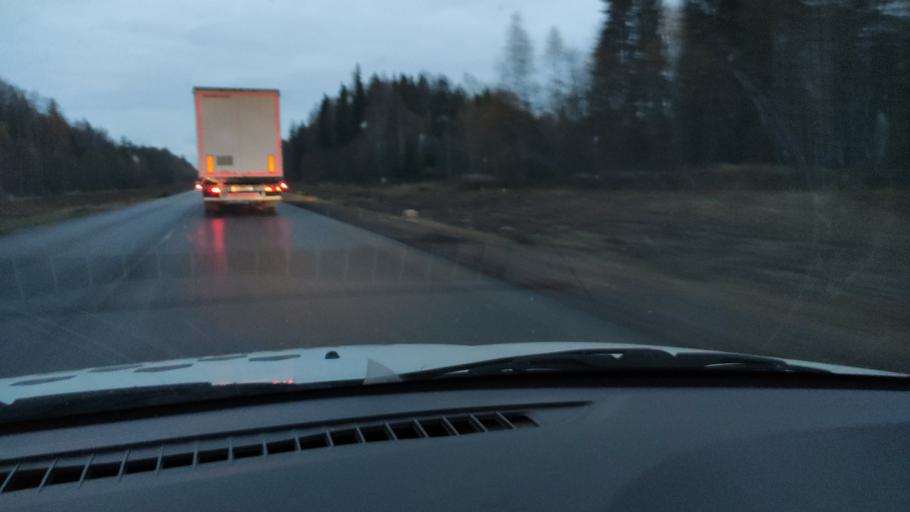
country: RU
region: Kirov
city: Kostino
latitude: 58.8208
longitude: 53.3530
